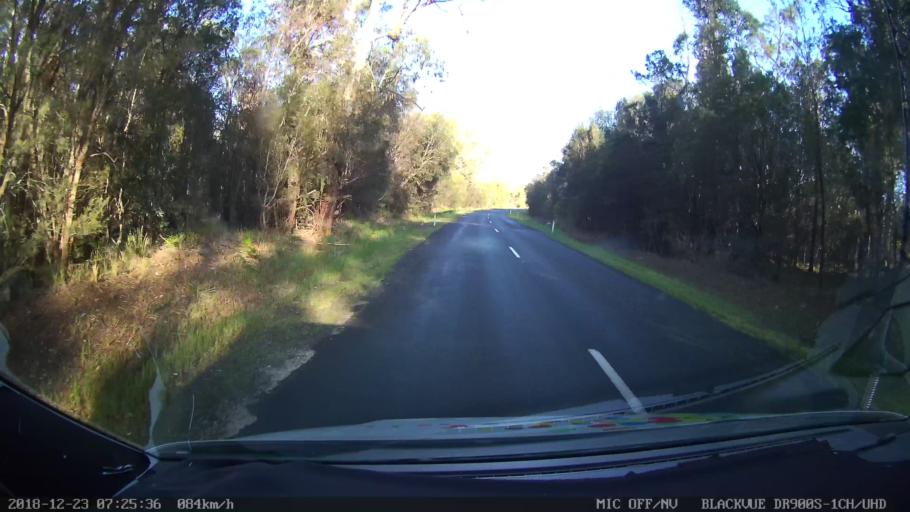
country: AU
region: New South Wales
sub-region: Armidale Dumaresq
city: Enmore
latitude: -30.4973
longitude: 152.2087
